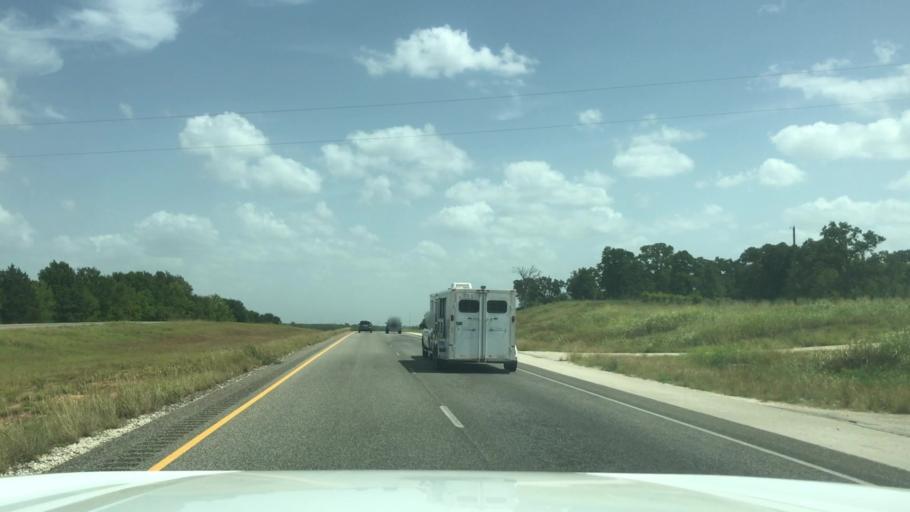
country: US
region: Texas
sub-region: Robertson County
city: Hearne
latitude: 30.9254
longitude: -96.6279
